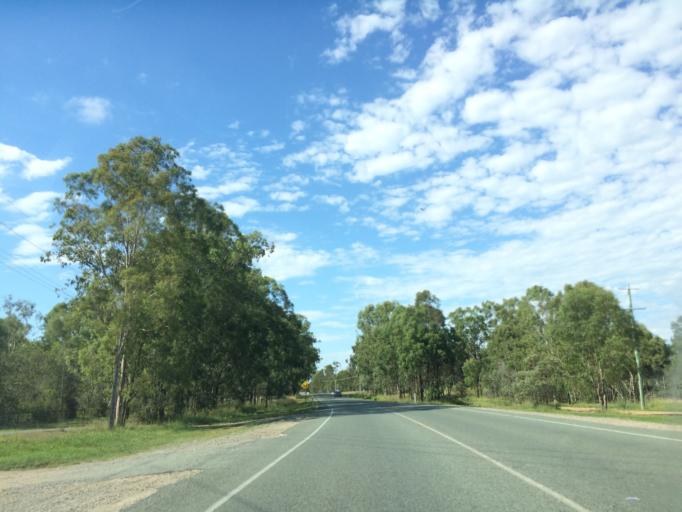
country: AU
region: Queensland
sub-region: Logan
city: Park Ridge South
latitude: -27.7248
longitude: 152.9848
